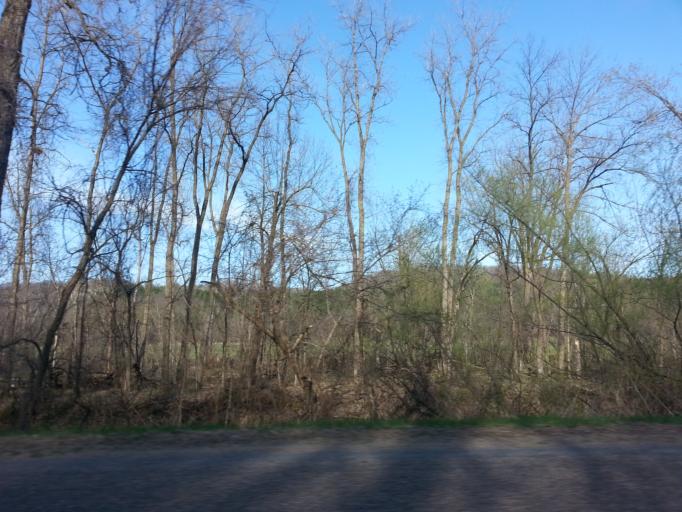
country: US
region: Minnesota
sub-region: Goodhue County
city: Red Wing
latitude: 44.6561
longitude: -92.5917
